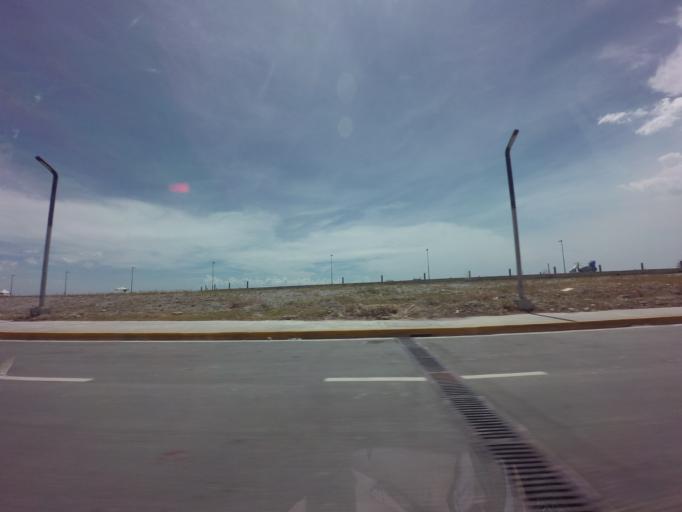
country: PH
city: Sambayanihan People's Village
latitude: 14.5132
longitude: 120.9779
